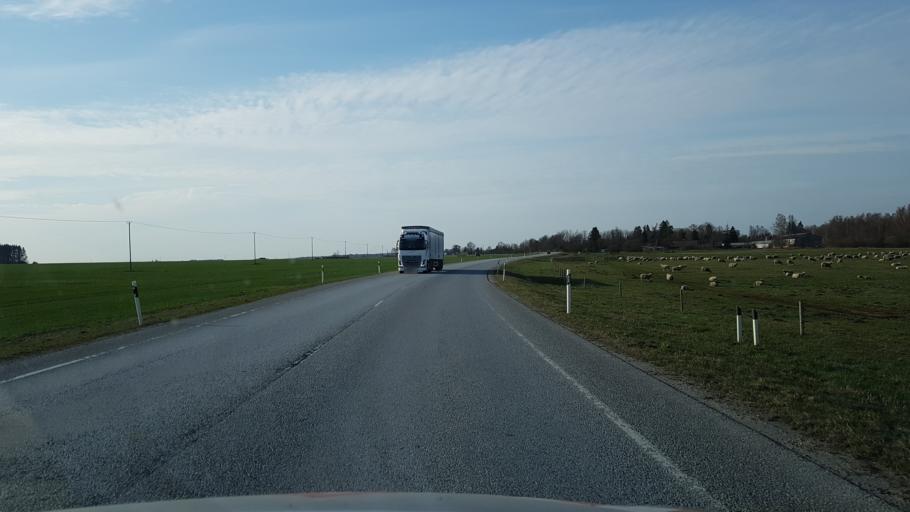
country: EE
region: Laeaene-Virumaa
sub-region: Haljala vald
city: Haljala
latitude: 59.4091
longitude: 26.2954
